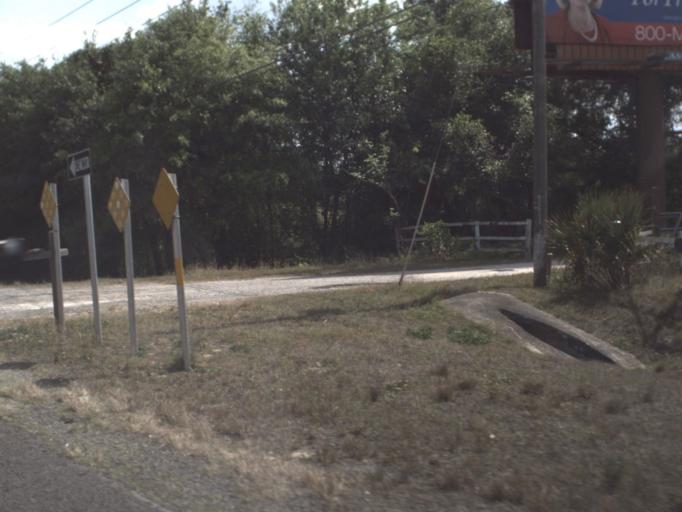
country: US
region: Florida
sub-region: Lake County
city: Minneola
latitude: 28.6233
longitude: -81.7609
